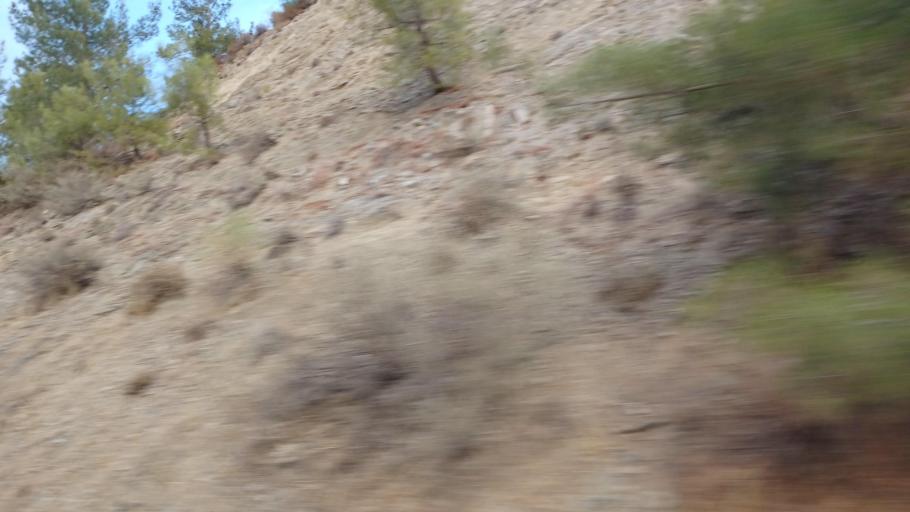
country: CY
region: Lefkosia
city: Kakopetria
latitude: 34.9834
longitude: 32.9060
